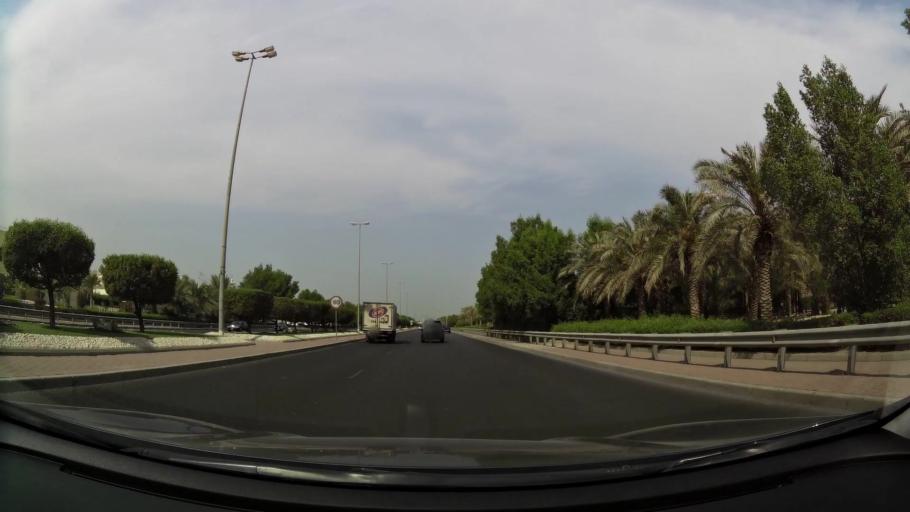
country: KW
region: Muhafazat Hawalli
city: Hawalli
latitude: 29.3129
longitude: 47.9967
